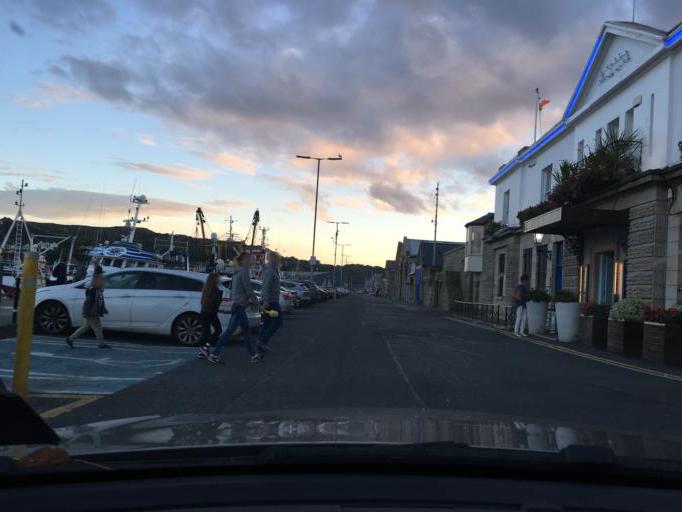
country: IE
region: Leinster
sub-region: Fingal County
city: Howth
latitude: 53.3923
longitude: -6.0692
